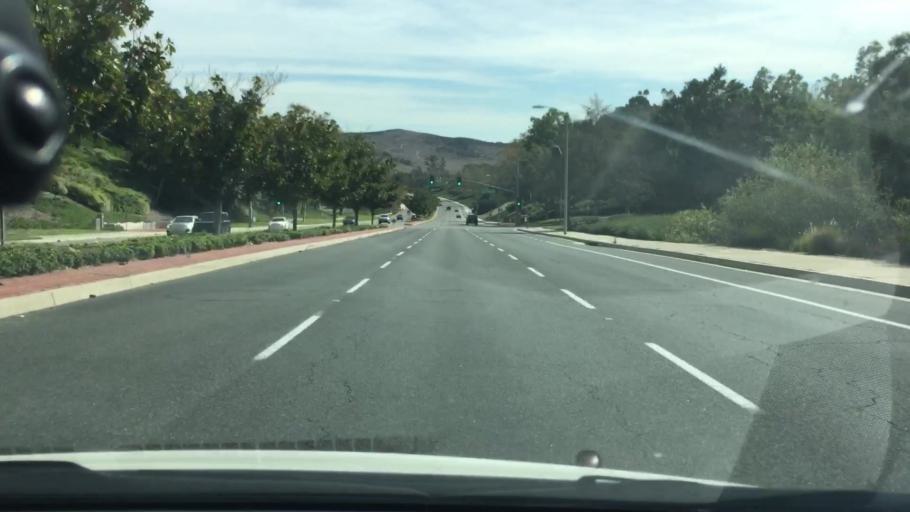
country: US
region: California
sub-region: Orange County
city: Rancho Santa Margarita
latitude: 33.6440
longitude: -117.6241
